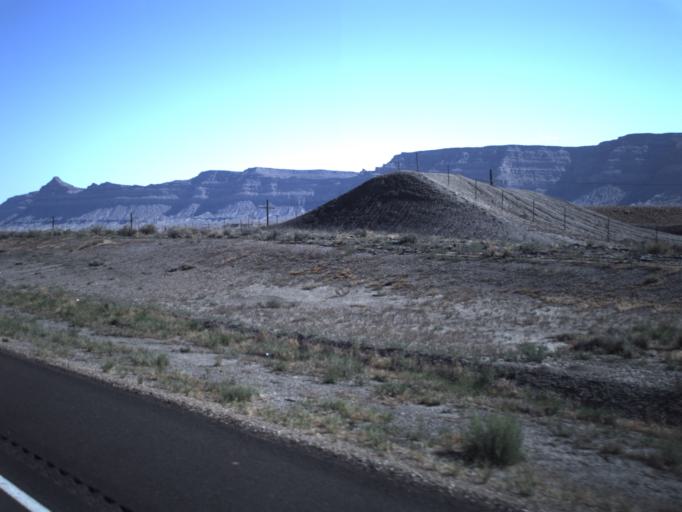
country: US
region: Utah
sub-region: Carbon County
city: East Carbon City
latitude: 39.0841
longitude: -110.3188
